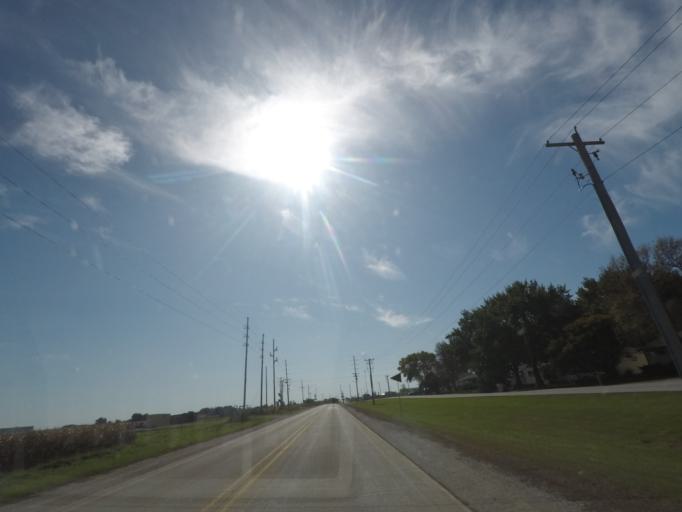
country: US
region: Iowa
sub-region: Story County
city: Nevada
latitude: 42.0179
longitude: -93.4347
